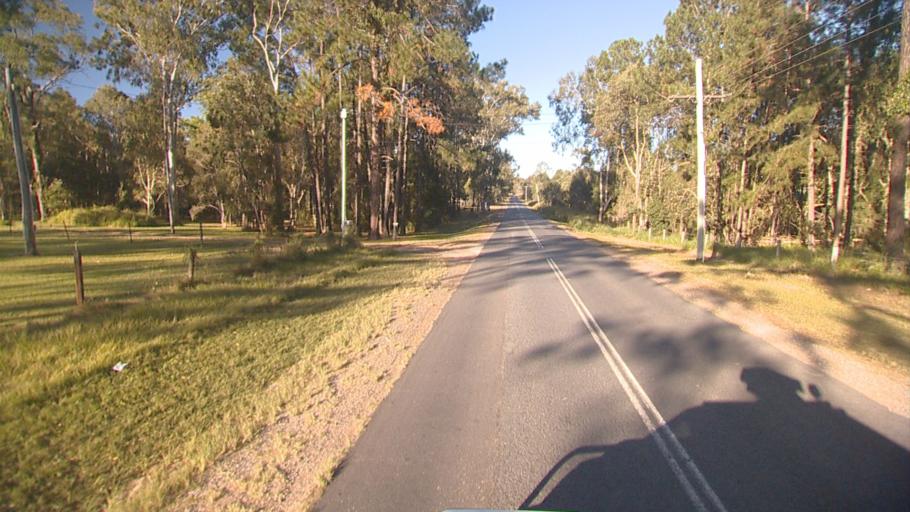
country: AU
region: Queensland
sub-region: Logan
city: North Maclean
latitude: -27.7587
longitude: 153.0375
